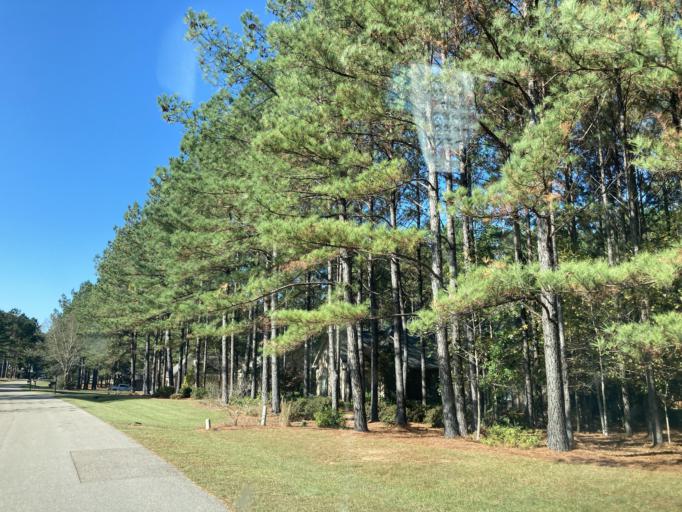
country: US
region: Mississippi
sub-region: Lamar County
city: Sumrall
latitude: 31.3345
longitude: -89.4866
